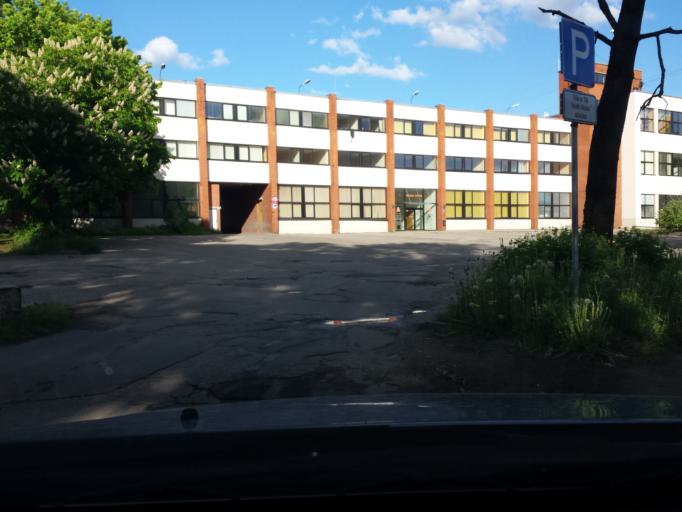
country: LV
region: Riga
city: Riga
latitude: 56.9800
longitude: 24.1530
